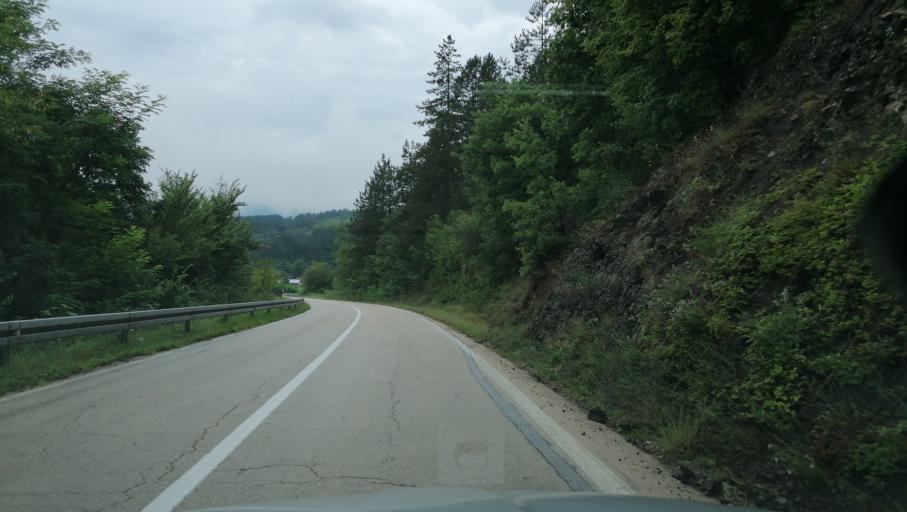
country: BA
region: Republika Srpska
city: Visegrad
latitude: 43.7862
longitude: 19.3356
